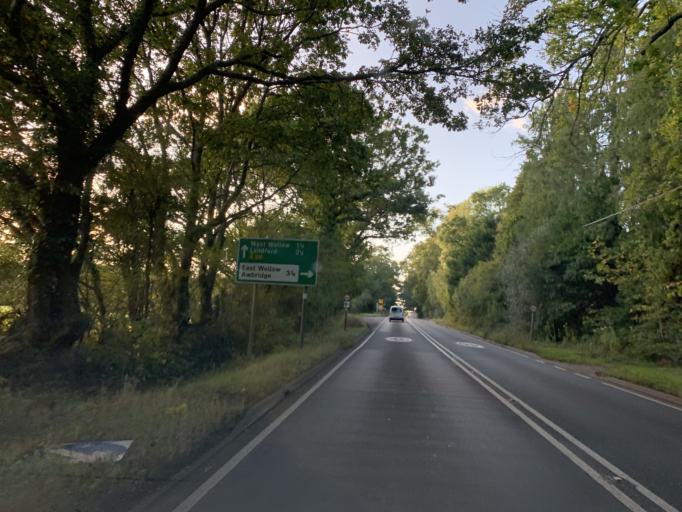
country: GB
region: England
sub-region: Hampshire
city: West Wellow
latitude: 50.9623
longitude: -1.5641
